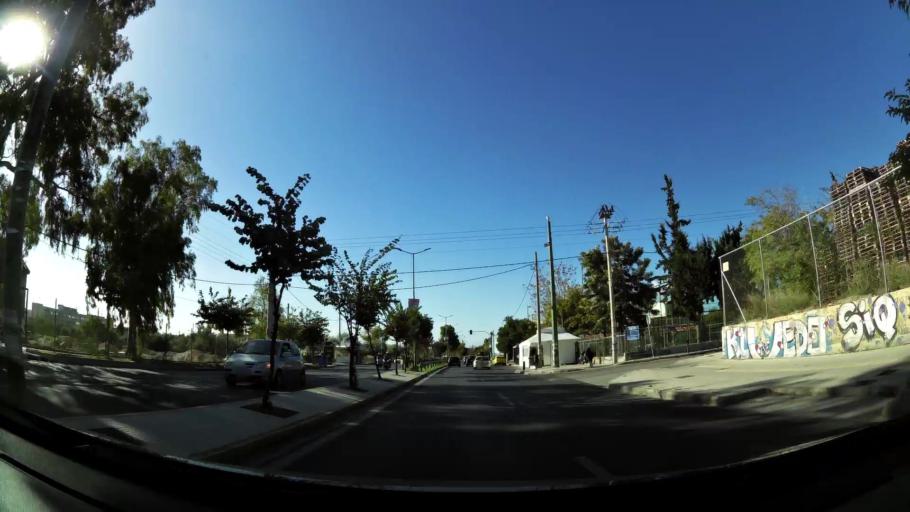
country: GR
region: Attica
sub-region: Nomarchia Athinas
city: Aigaleo
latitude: 37.9805
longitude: 23.6709
